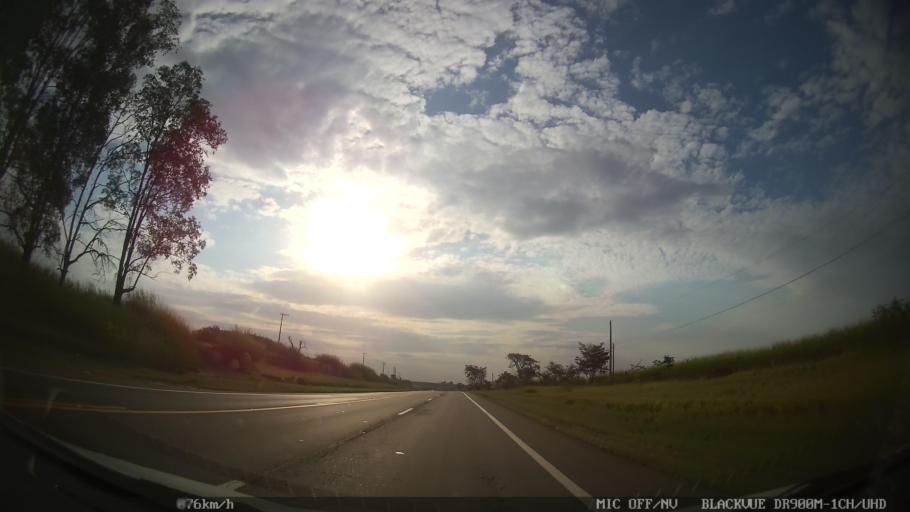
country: BR
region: Sao Paulo
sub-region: Cosmopolis
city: Cosmopolis
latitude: -22.6274
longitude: -47.2115
